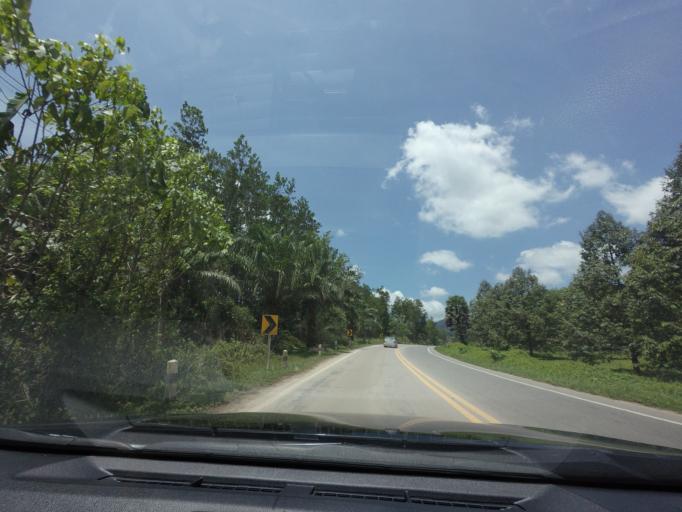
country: TH
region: Chumphon
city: Ban Nam Yuen
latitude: 9.9028
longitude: 98.8953
